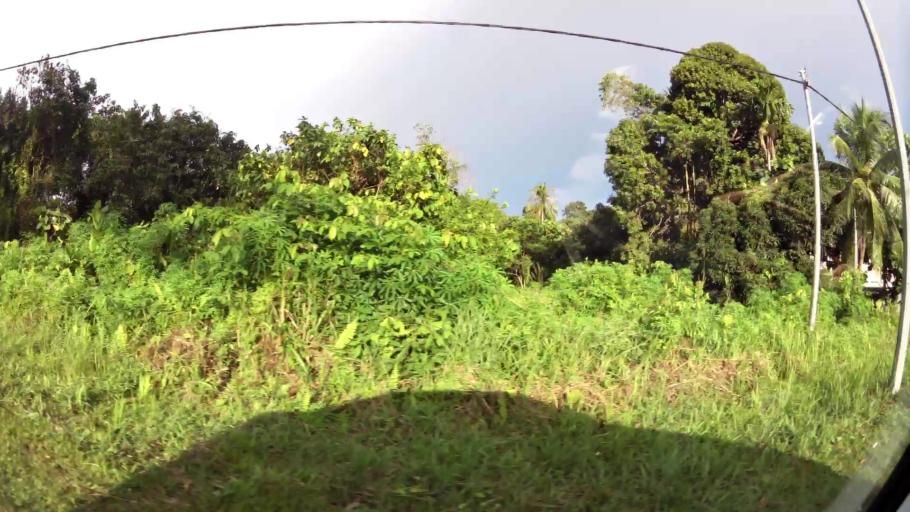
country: BN
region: Brunei and Muara
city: Bandar Seri Begawan
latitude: 4.9632
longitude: 115.0206
